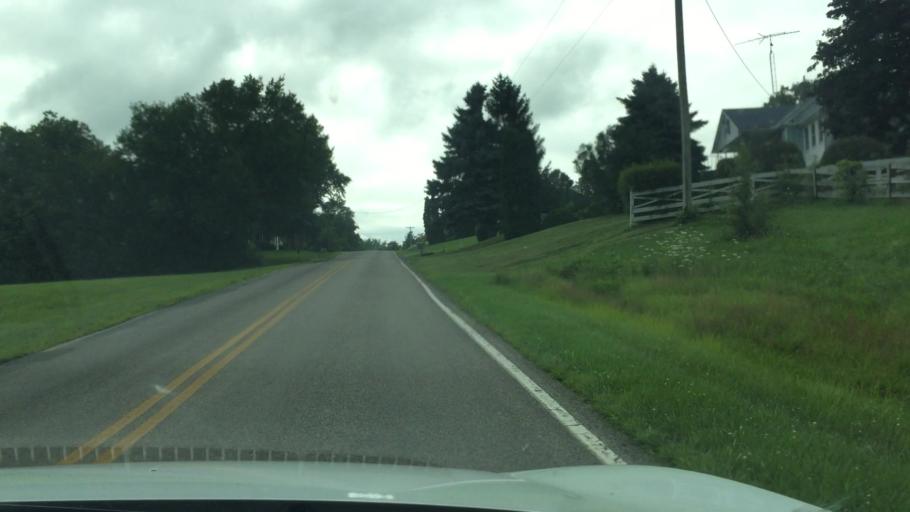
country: US
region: Ohio
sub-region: Champaign County
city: Mechanicsburg
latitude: 40.0602
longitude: -83.6327
